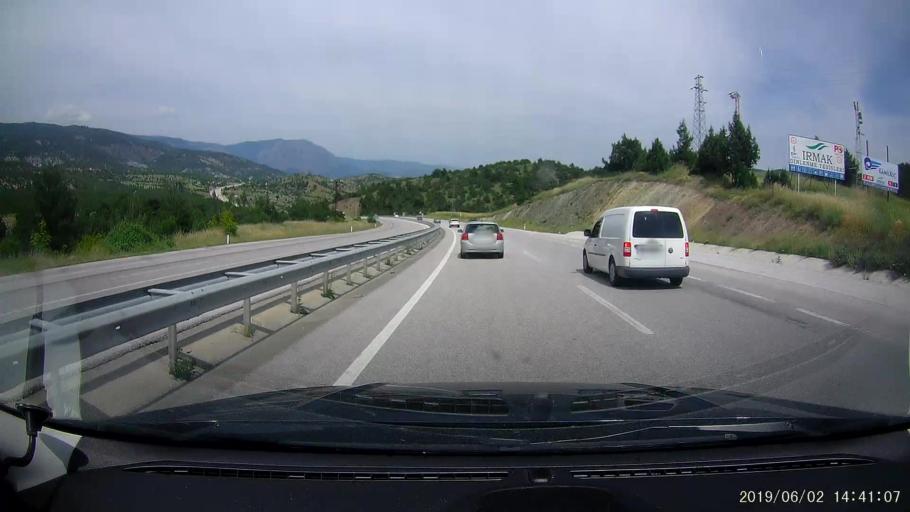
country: TR
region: Corum
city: Hacihamza
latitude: 41.0827
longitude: 34.3335
